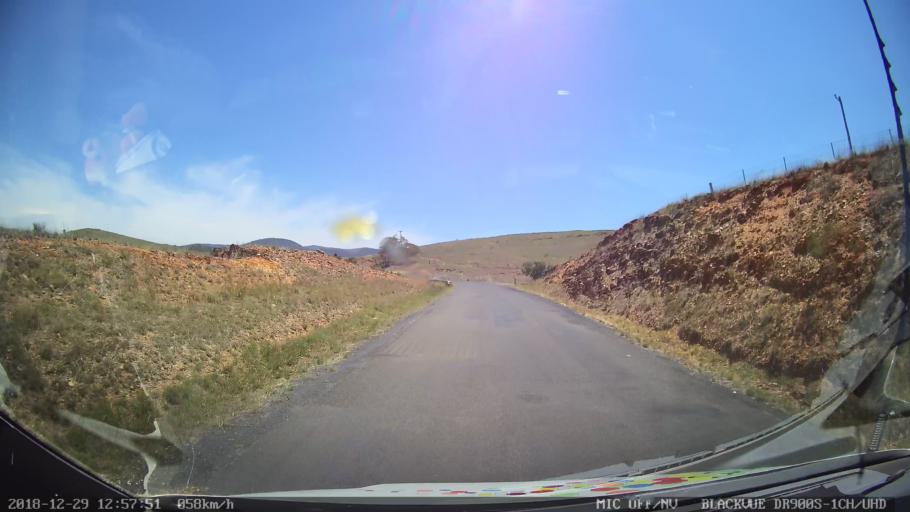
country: AU
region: Australian Capital Territory
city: Macarthur
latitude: -35.7097
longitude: 149.1733
